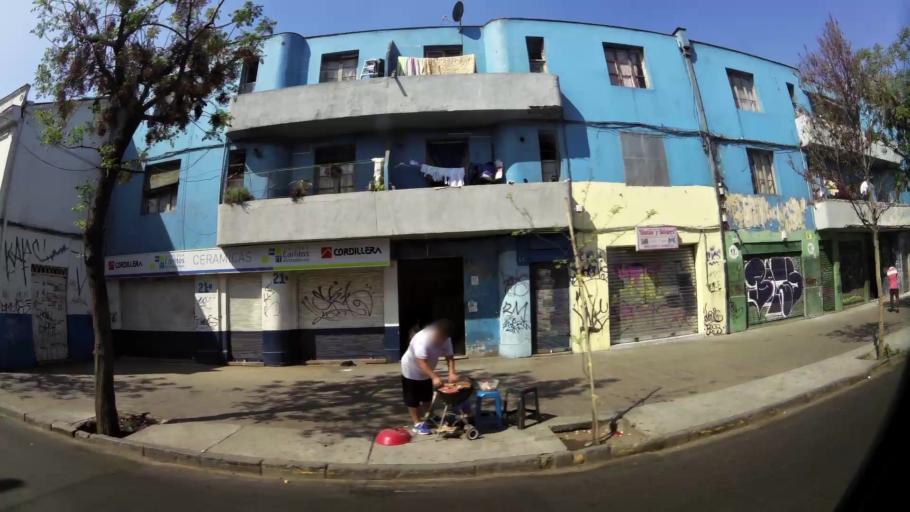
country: CL
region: Santiago Metropolitan
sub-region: Provincia de Santiago
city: Santiago
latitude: -33.4492
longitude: -70.6779
